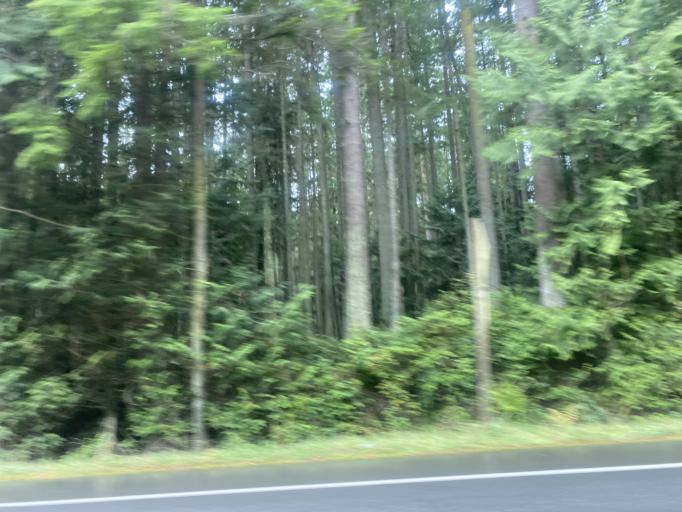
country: US
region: Washington
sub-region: Island County
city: Freeland
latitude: 48.0295
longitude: -122.5068
